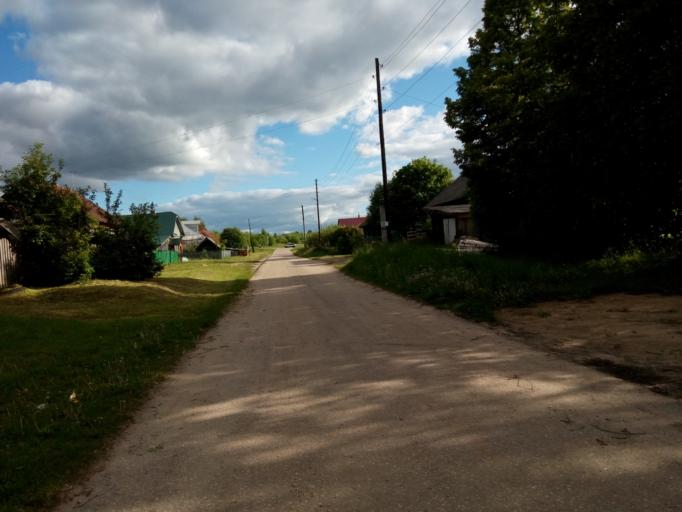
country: RU
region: Nizjnij Novgorod
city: Voskresenskoye
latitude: 56.7825
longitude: 45.5122
